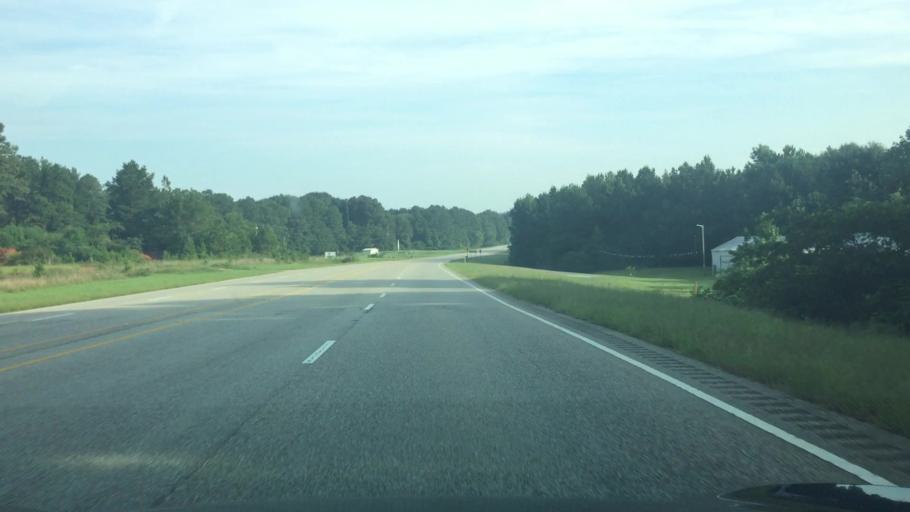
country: US
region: Alabama
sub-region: Covington County
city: Andalusia
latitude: 31.4189
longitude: -86.6097
